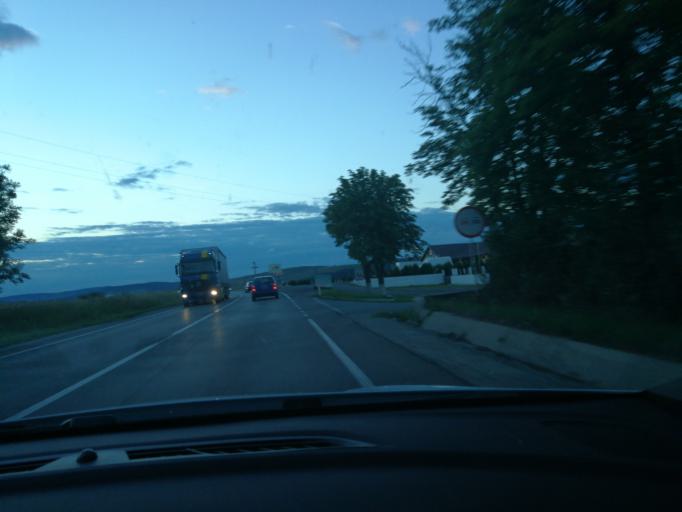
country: RO
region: Brasov
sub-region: Comuna Homorod
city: Homorod
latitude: 46.0257
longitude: 25.2605
